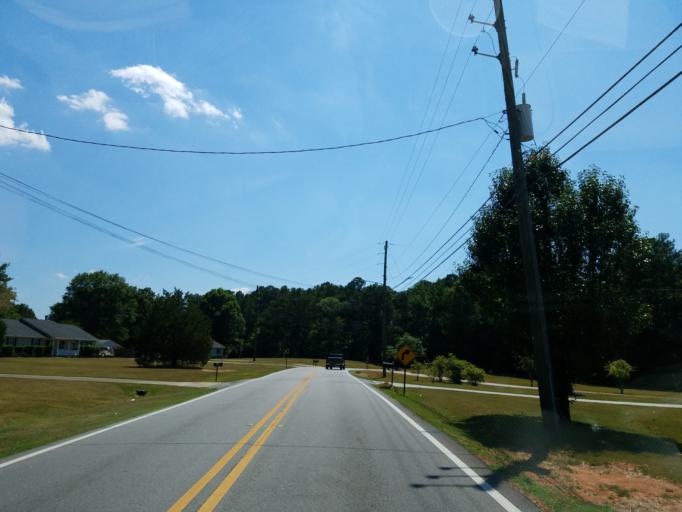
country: US
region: Georgia
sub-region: Henry County
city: Stockbridge
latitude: 33.4780
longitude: -84.2490
